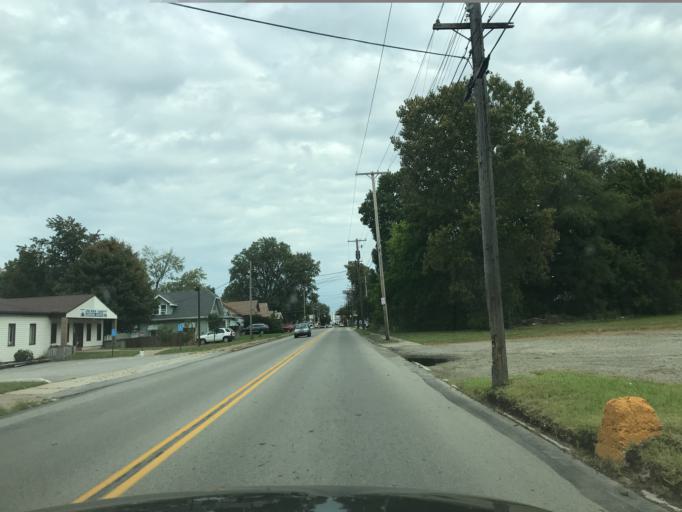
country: US
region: Pennsylvania
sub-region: Erie County
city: Wesleyville
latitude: 42.1331
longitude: -80.0317
